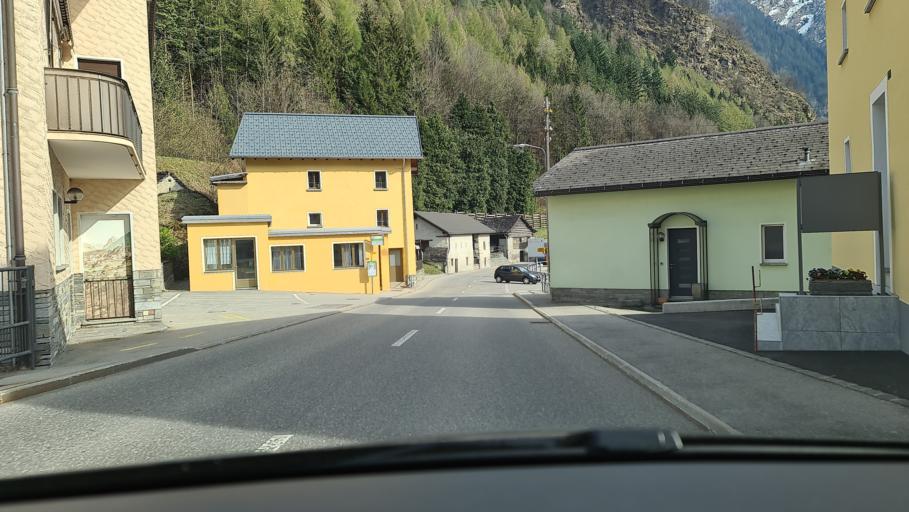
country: CH
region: Ticino
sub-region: Blenio District
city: Acquarossa
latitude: 46.5033
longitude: 8.9496
